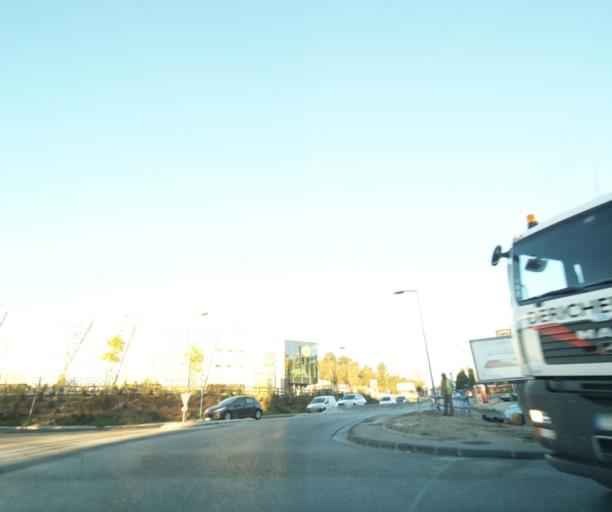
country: FR
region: Provence-Alpes-Cote d'Azur
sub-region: Departement des Bouches-du-Rhone
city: Allauch
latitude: 43.3006
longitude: 5.4771
